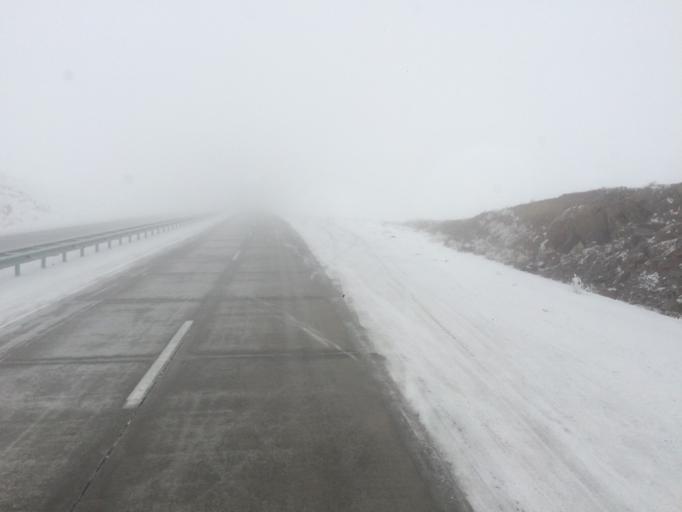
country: KZ
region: Zhambyl
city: Georgiyevka
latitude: 43.4274
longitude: 74.9582
